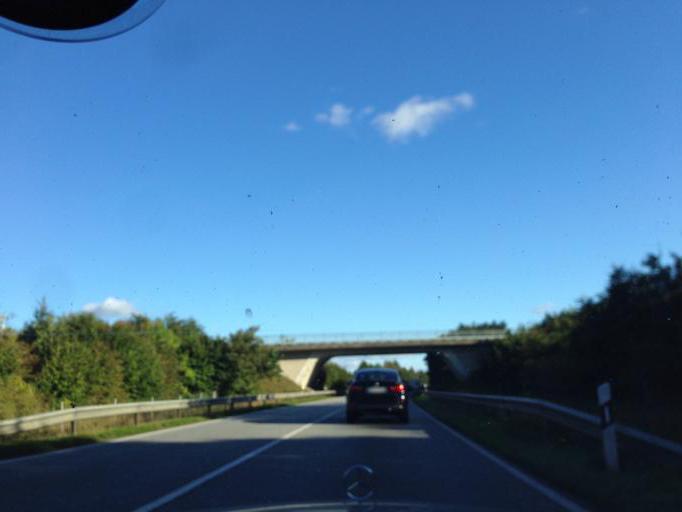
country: DE
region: Schleswig-Holstein
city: Latendorf
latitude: 54.0235
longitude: 10.0618
